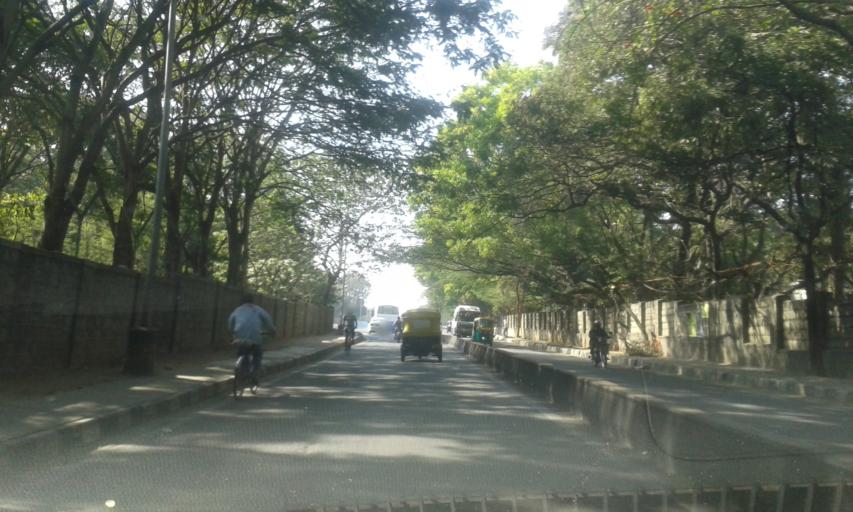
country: IN
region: Karnataka
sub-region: Bangalore Urban
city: Bangalore
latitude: 13.0125
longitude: 77.5683
